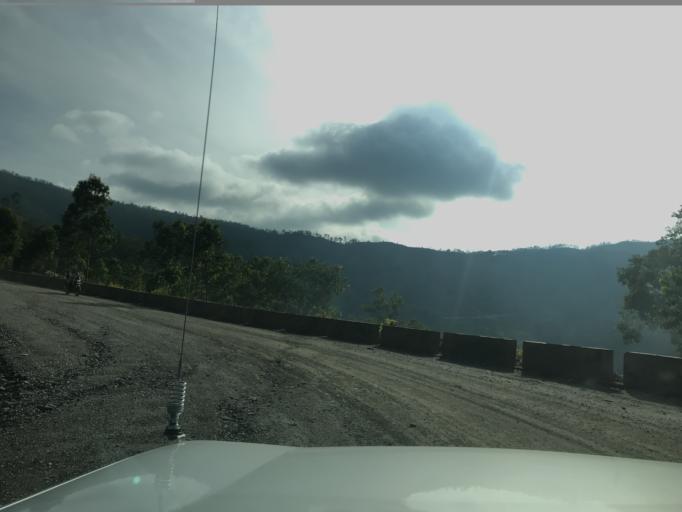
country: TL
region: Aileu
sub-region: Aileu Villa
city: Aileu
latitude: -8.6643
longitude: 125.5423
